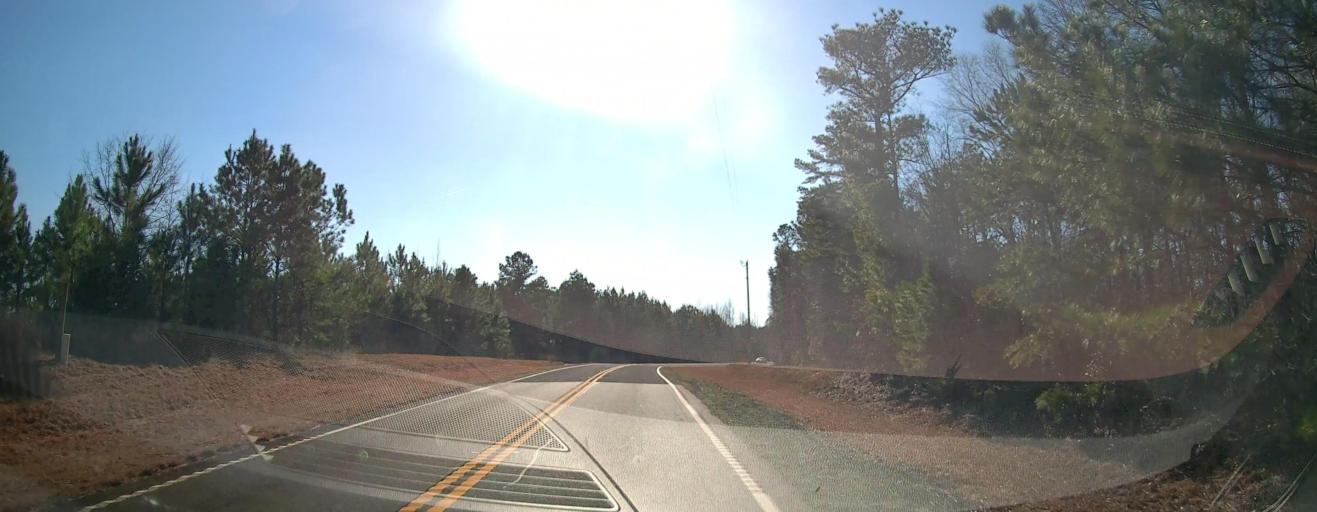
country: US
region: Georgia
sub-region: Talbot County
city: Talbotton
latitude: 32.6453
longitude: -84.4277
